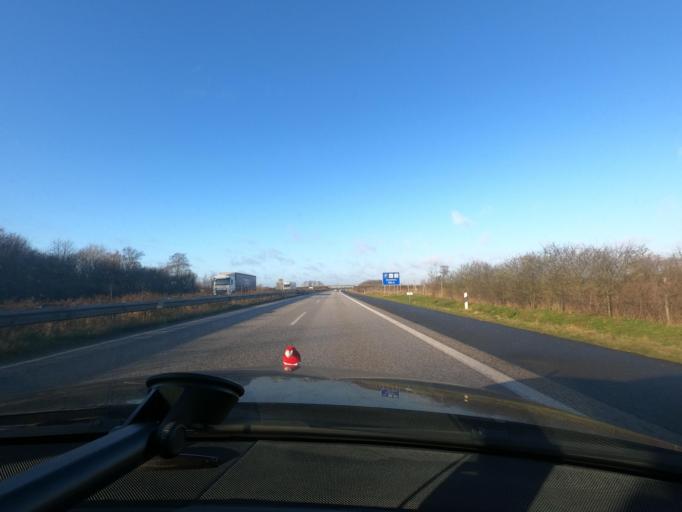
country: DE
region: Schleswig-Holstein
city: Schuby
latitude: 54.5308
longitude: 9.4804
